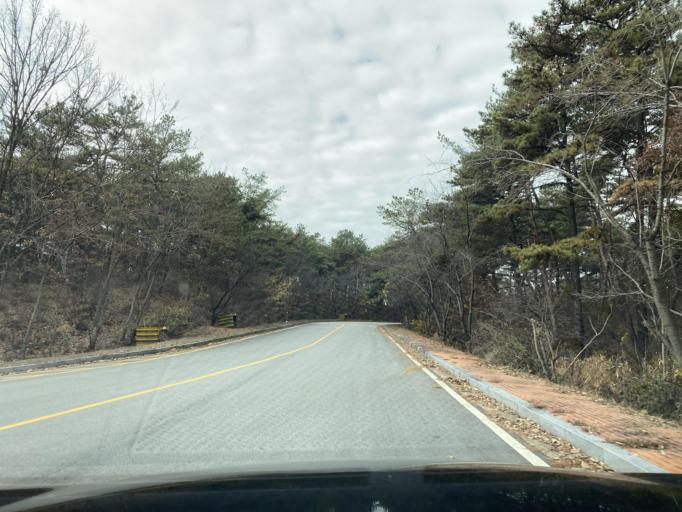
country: KR
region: Chungcheongnam-do
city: Hongsung
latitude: 36.6544
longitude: 126.6210
